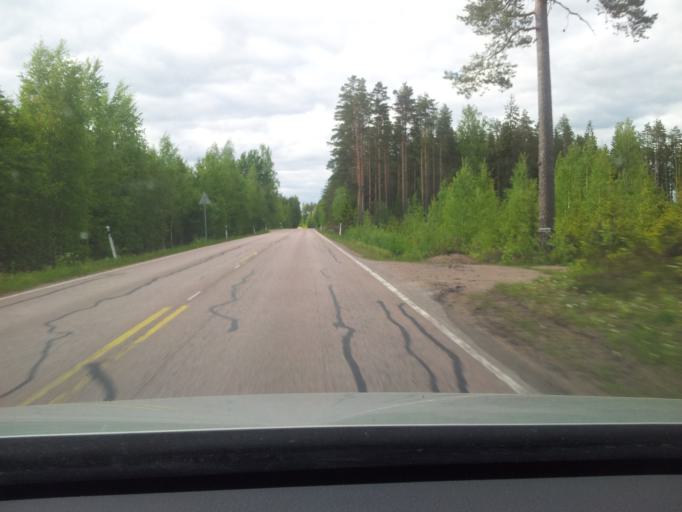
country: FI
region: South Karelia
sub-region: Lappeenranta
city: Luumaeki
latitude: 60.9522
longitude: 27.5787
